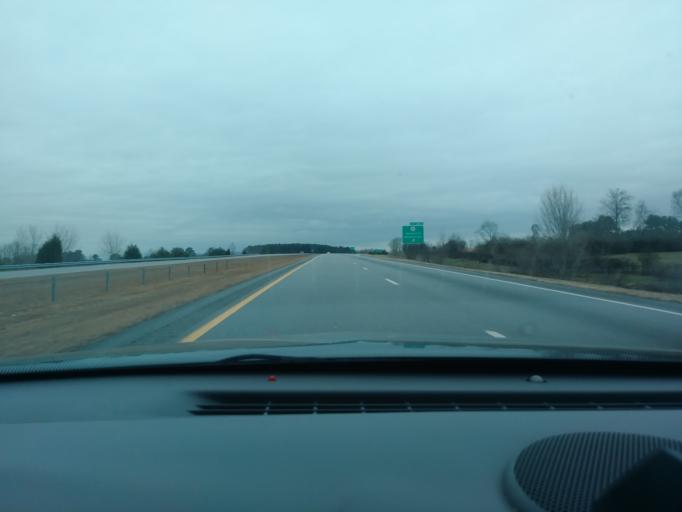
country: US
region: North Carolina
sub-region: Yadkin County
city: Yadkinville
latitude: 36.1169
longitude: -80.7653
